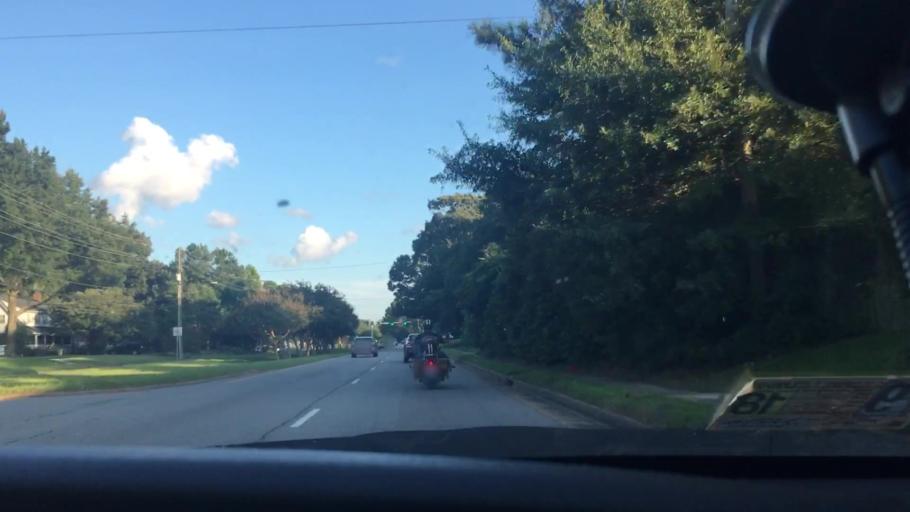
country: US
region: Virginia
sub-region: City of Chesapeake
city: Chesapeake
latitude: 36.8860
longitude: -76.1357
